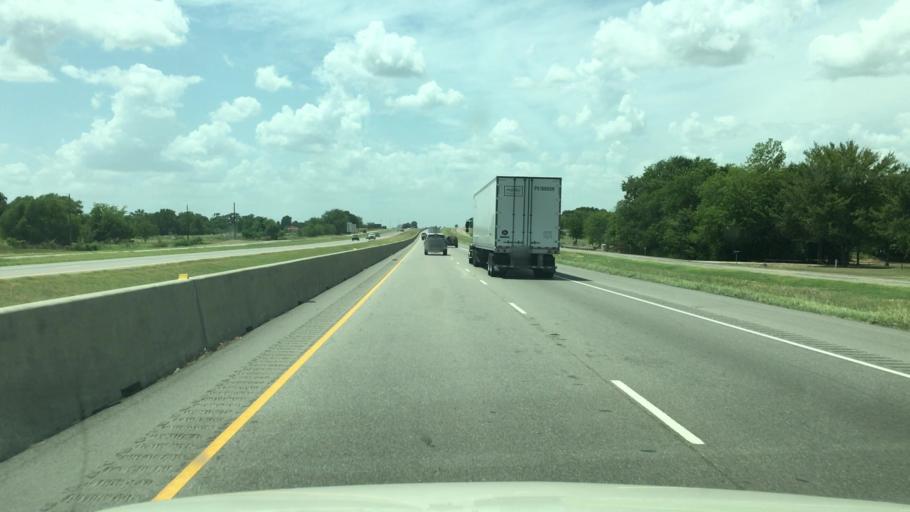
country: US
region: Texas
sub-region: Franklin County
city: Mount Vernon
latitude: 33.1632
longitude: -95.2554
